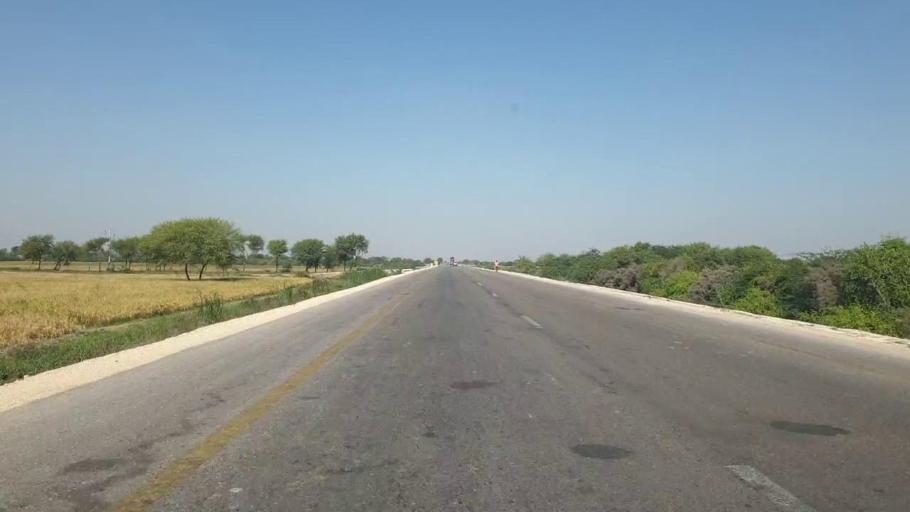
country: PK
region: Sindh
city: Talhar
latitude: 24.8235
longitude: 68.8159
